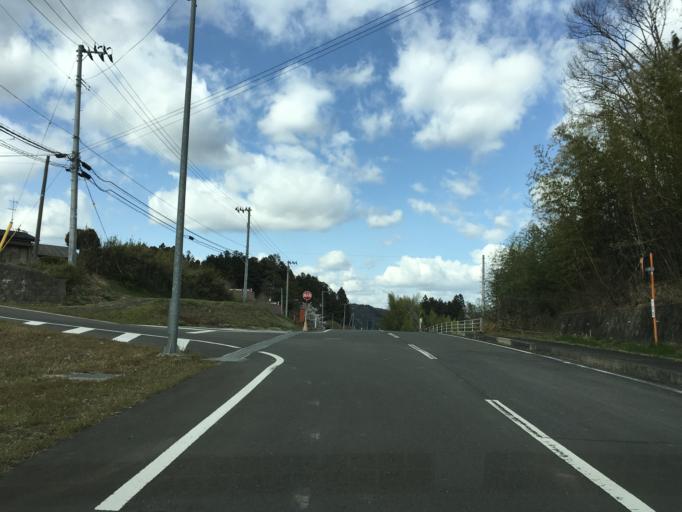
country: JP
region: Iwate
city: Ichinoseki
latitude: 38.7503
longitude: 141.2662
